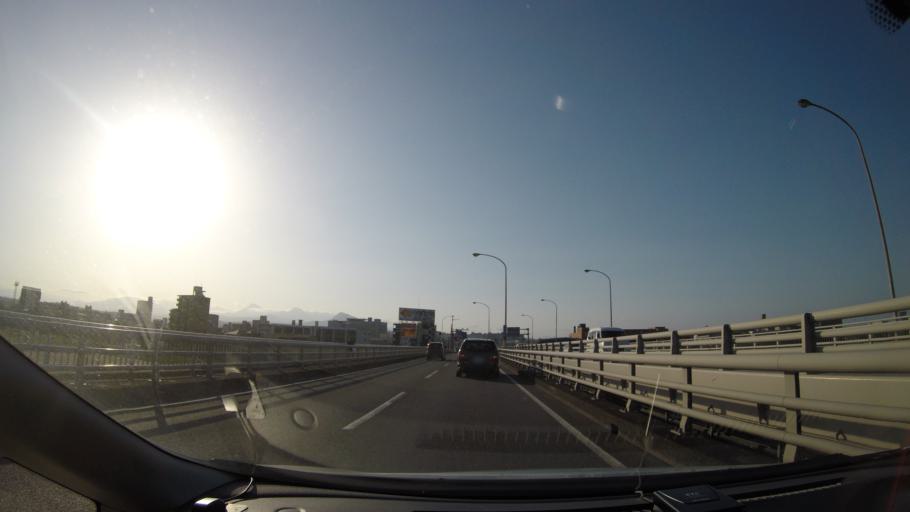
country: JP
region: Oita
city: Oita
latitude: 33.2030
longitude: 131.6051
